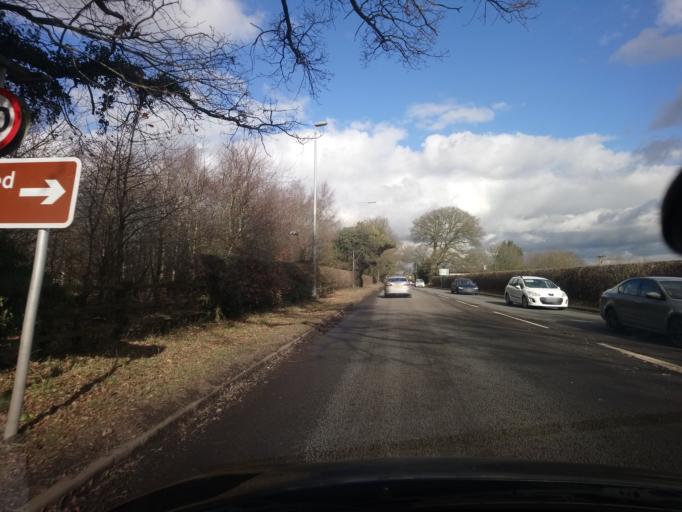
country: GB
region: England
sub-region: Cheshire West and Chester
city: Oakmere
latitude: 53.2007
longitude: -2.6304
